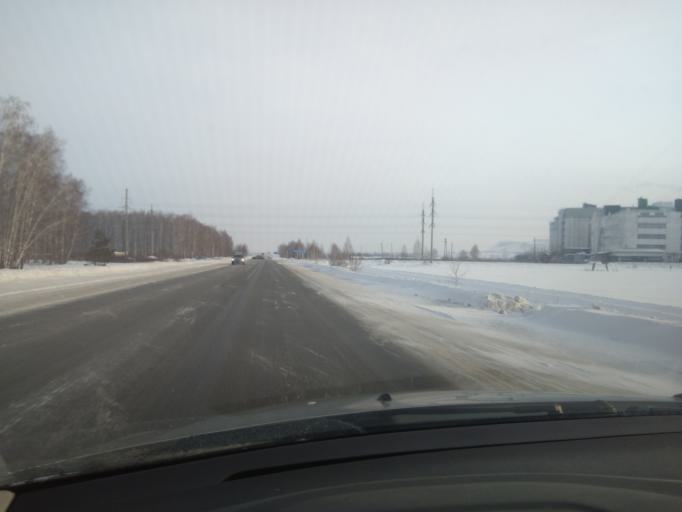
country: RU
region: Sverdlovsk
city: Bogdanovich
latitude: 56.8065
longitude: 62.0312
